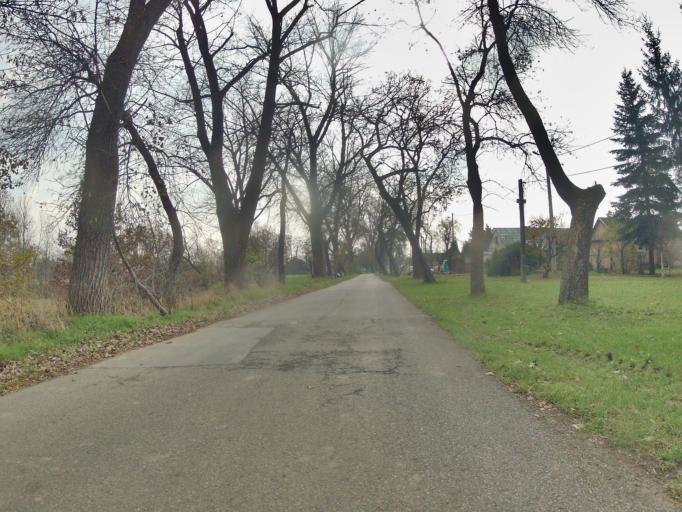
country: PL
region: Lesser Poland Voivodeship
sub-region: Powiat wielicki
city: Wegrzce Wielkie
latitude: 50.0574
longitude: 20.1118
